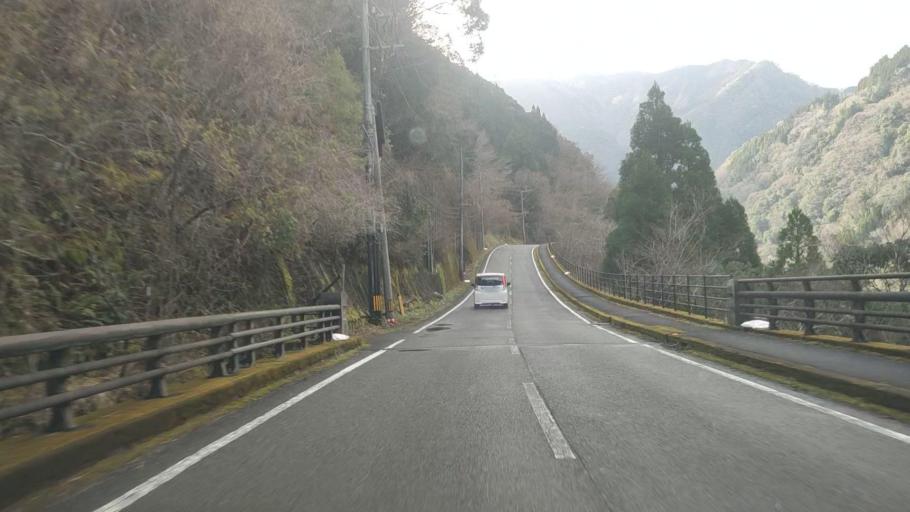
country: JP
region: Kumamoto
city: Hitoyoshi
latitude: 32.4085
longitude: 130.8293
